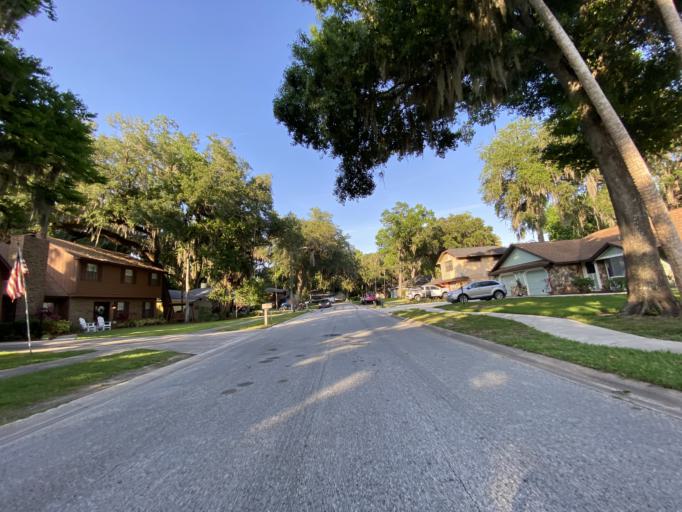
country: US
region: Florida
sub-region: Volusia County
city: Port Orange
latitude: 29.1440
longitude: -81.0100
